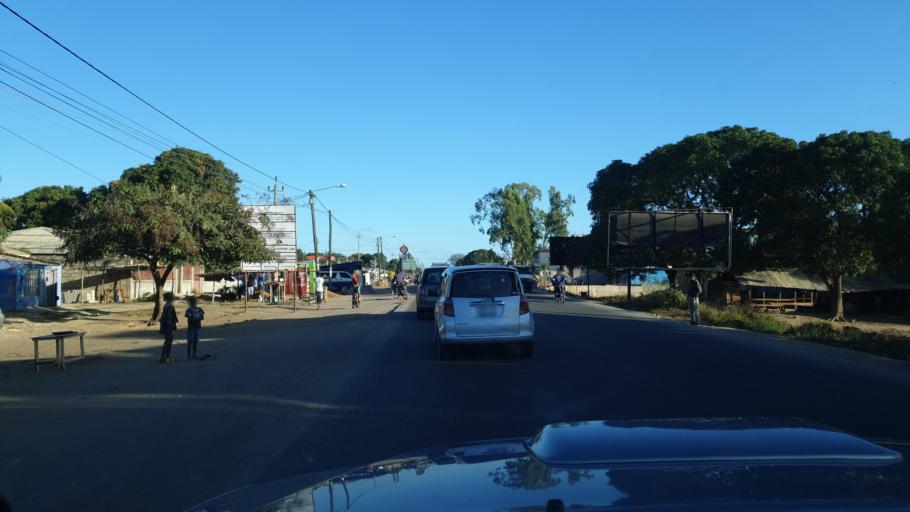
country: MZ
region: Nampula
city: Nacala
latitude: -14.5759
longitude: 40.6816
